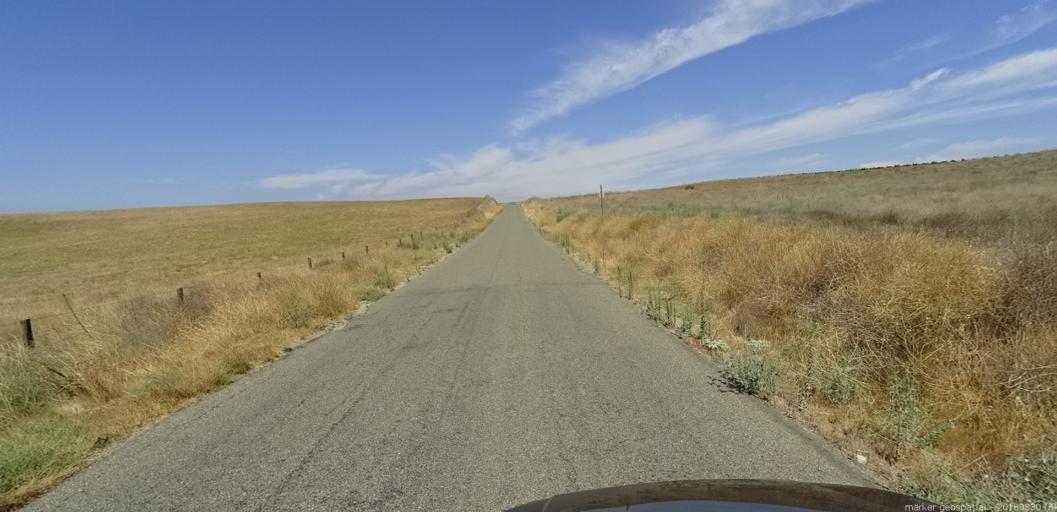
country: US
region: California
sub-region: Monterey County
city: King City
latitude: 36.1107
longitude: -121.0567
